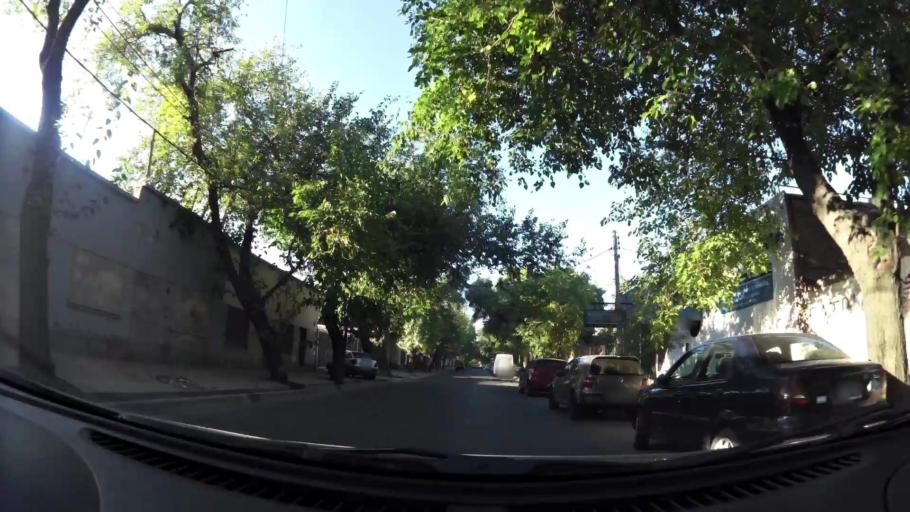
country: AR
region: Mendoza
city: Mendoza
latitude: -32.8723
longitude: -68.8293
